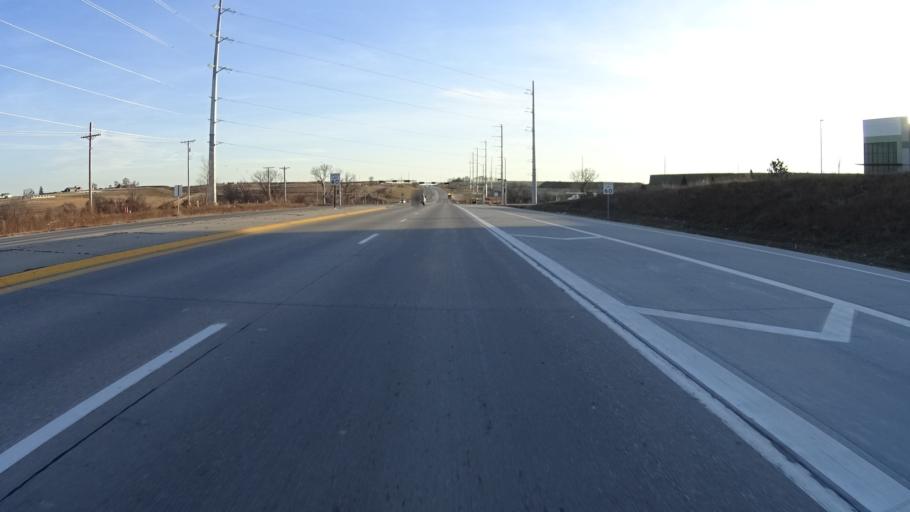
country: US
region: Nebraska
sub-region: Sarpy County
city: Chalco
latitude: 41.1417
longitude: -96.1391
